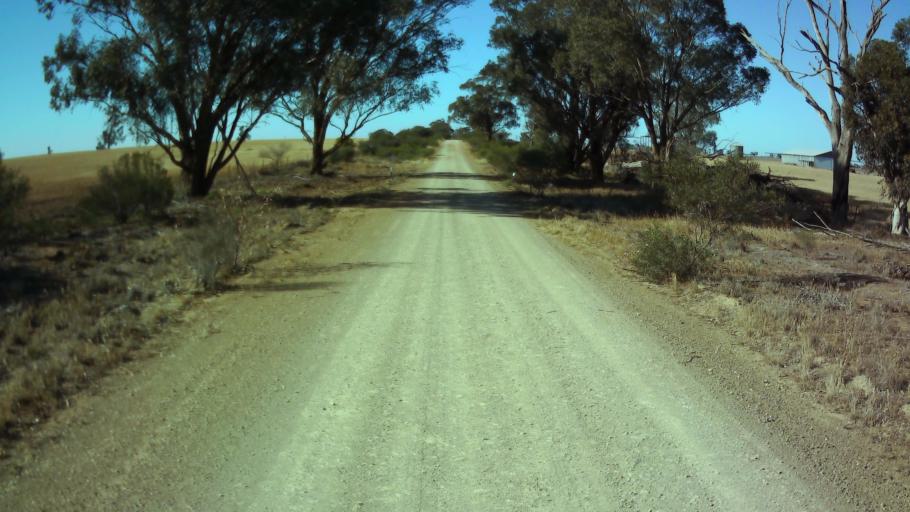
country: AU
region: New South Wales
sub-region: Weddin
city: Grenfell
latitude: -33.8808
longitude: 147.8824
